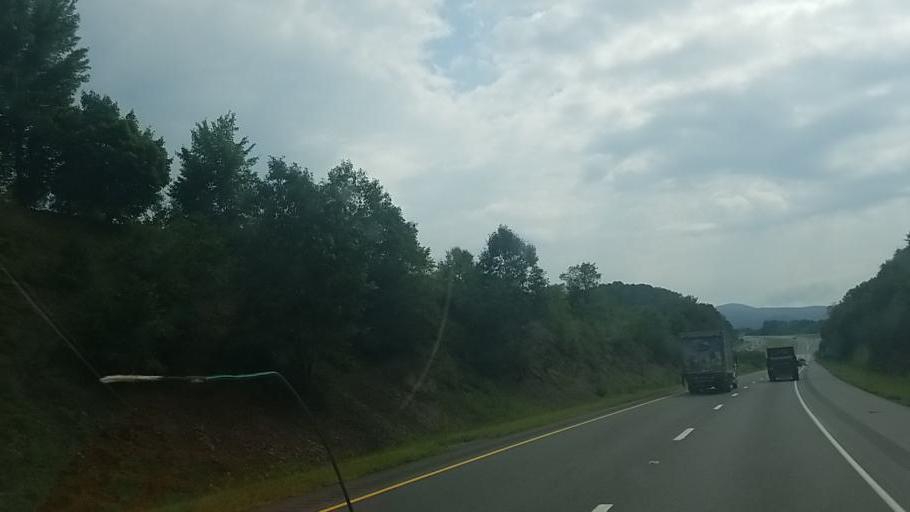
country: US
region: Pennsylvania
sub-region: Perry County
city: Newport
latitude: 40.5700
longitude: -77.2405
